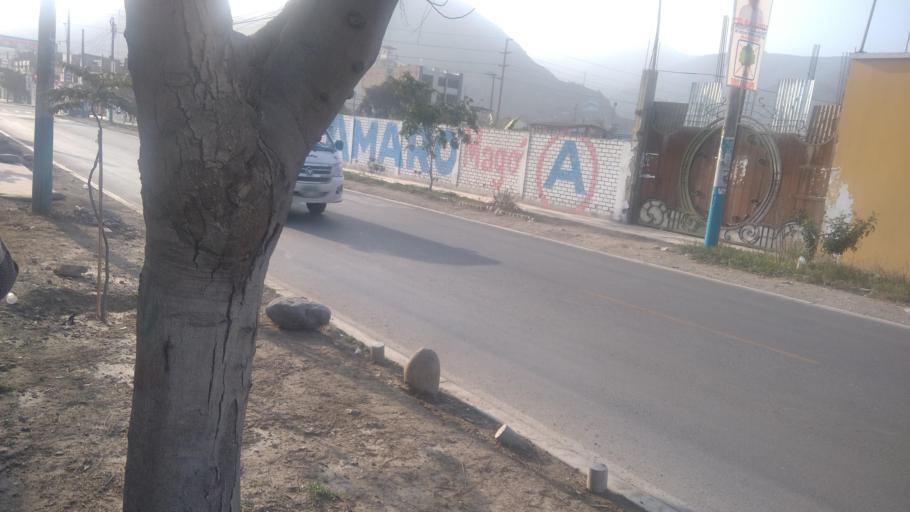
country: PE
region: Lima
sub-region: Lima
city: Vitarte
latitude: -12.0175
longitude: -76.9460
